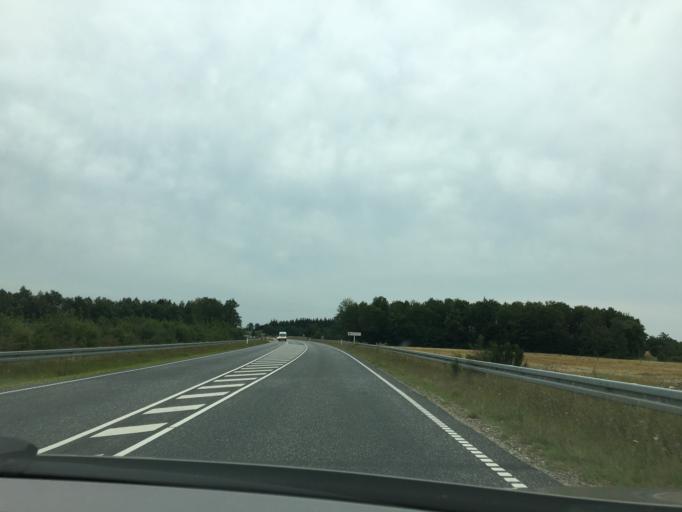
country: DK
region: Central Jutland
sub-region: Herning Kommune
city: Sunds
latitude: 56.2048
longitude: 8.9903
